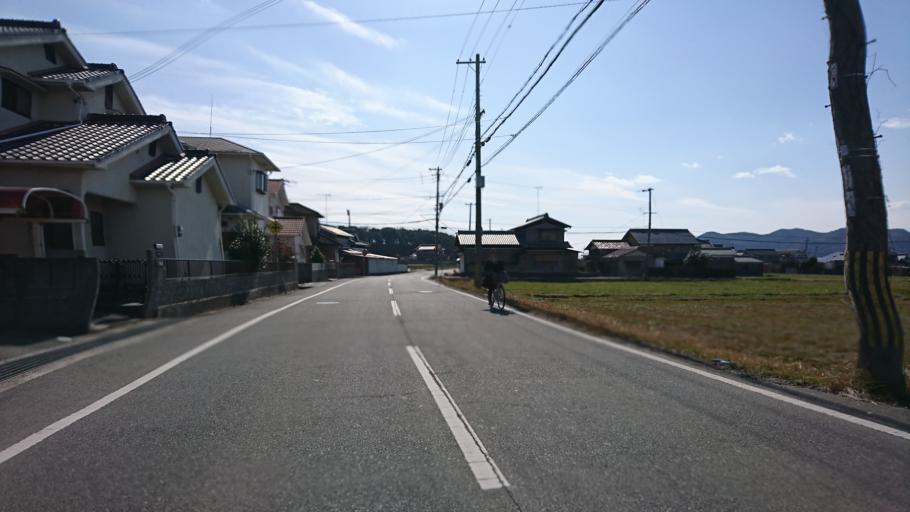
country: JP
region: Hyogo
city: Kakogawacho-honmachi
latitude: 34.8132
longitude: 134.8277
